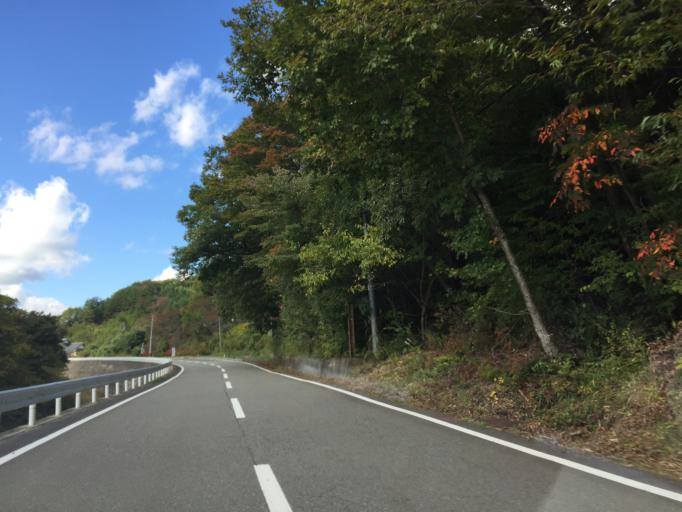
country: JP
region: Fukushima
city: Namie
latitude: 37.5655
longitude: 140.8026
